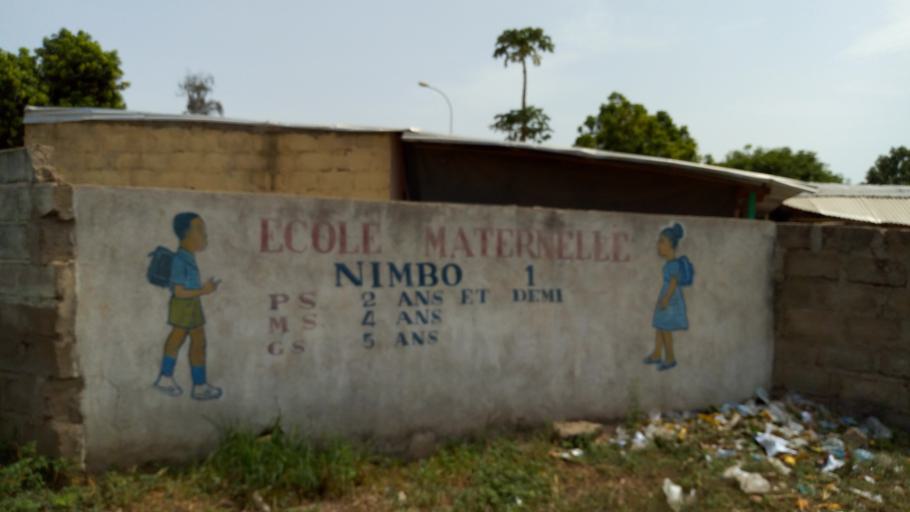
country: CI
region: Vallee du Bandama
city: Bouake
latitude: 7.6774
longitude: -5.0246
